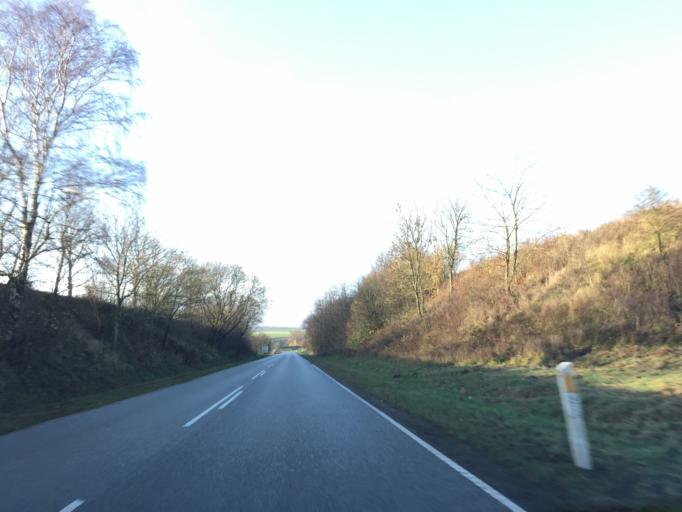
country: DK
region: Central Jutland
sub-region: Skanderborg Kommune
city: Galten
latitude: 56.1754
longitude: 9.8464
